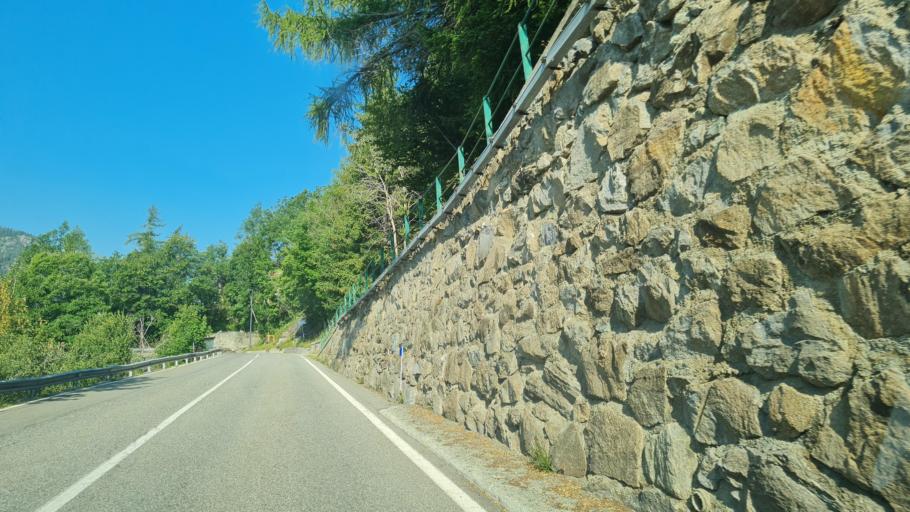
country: IT
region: Aosta Valley
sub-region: Valle d'Aosta
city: Champorcher
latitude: 45.6247
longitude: 7.6260
